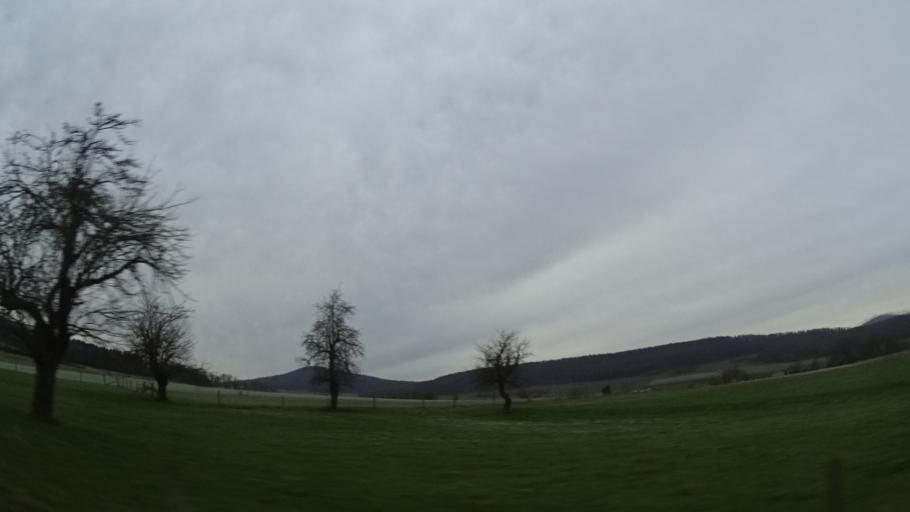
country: DE
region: Hesse
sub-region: Regierungsbezirk Kassel
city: Rasdorf
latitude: 50.7334
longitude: 9.9212
